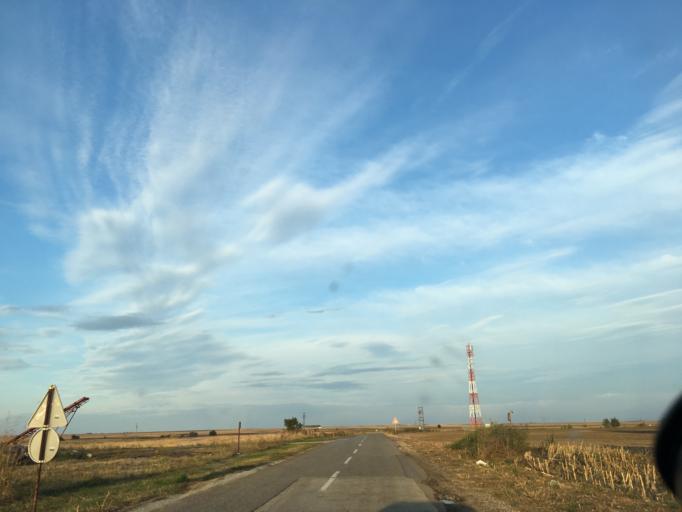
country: RS
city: Vladimirovac
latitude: 44.9020
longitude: 20.8960
